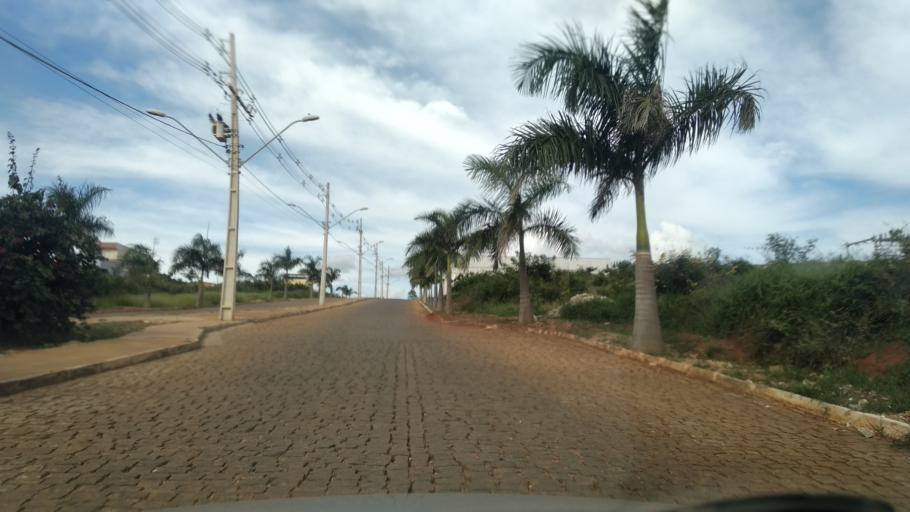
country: BR
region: Bahia
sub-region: Caetite
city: Caetite
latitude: -14.0589
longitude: -42.4946
